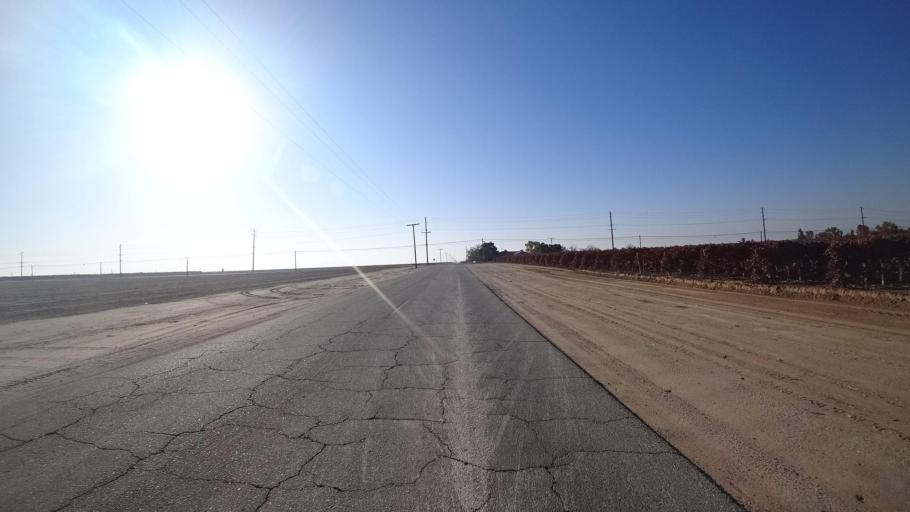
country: US
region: California
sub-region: Tulare County
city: Richgrove
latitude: 35.7772
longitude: -119.1696
